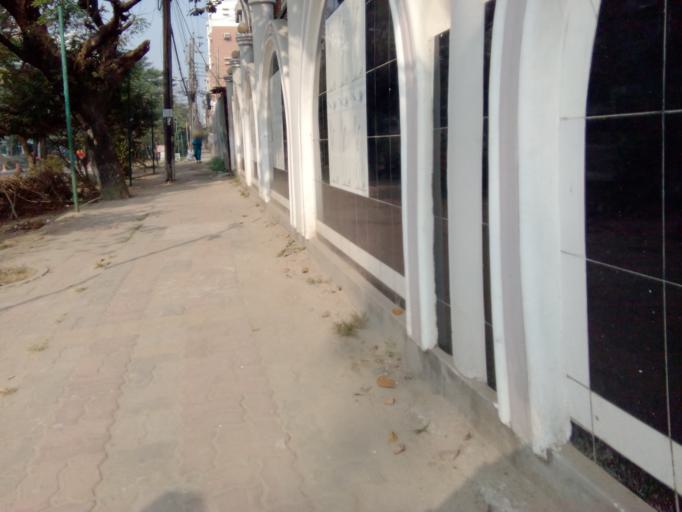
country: BD
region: Dhaka
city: Tungi
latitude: 23.8174
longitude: 90.4300
